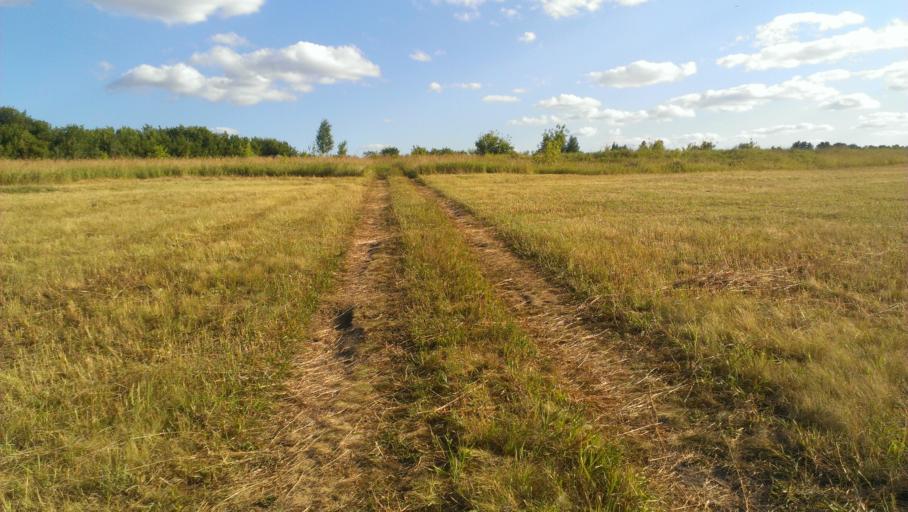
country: RU
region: Altai Krai
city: Gon'ba
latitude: 53.3887
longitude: 83.5991
